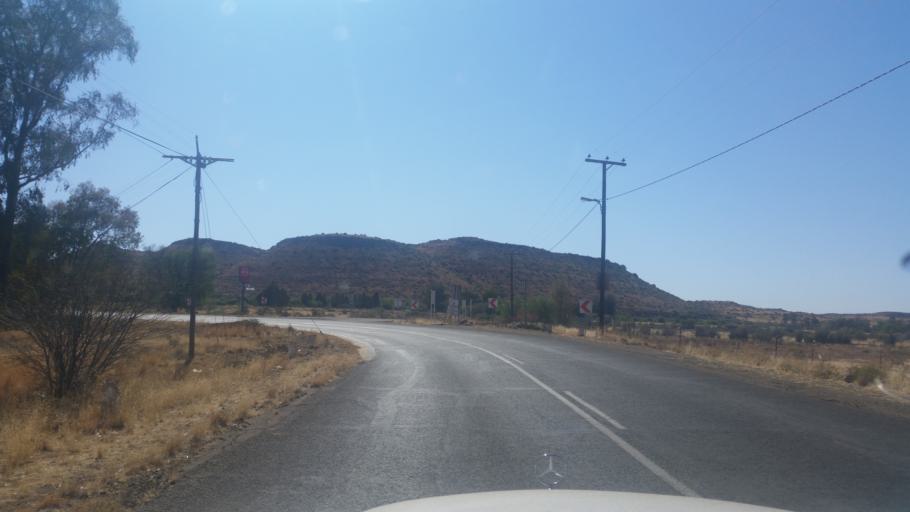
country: ZA
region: Orange Free State
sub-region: Xhariep District Municipality
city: Trompsburg
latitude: -30.4956
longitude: 25.9960
